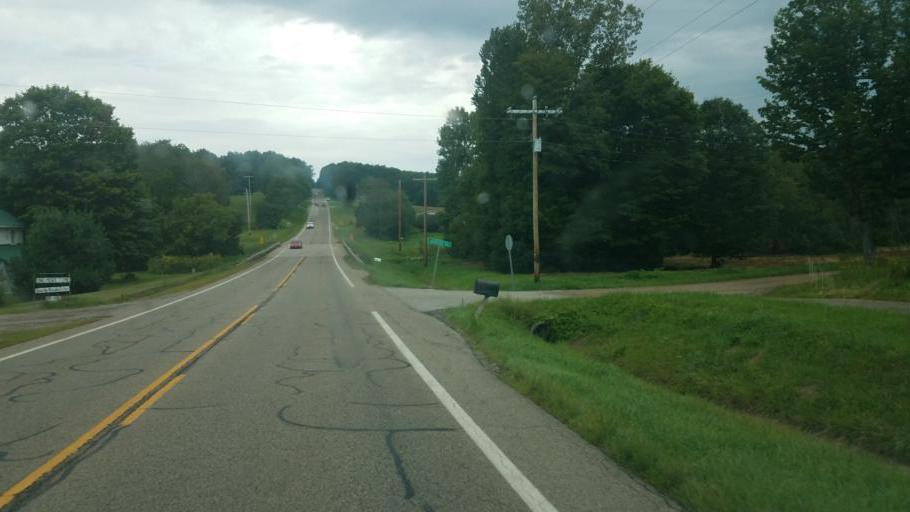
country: US
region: Ohio
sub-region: Knox County
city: Gambier
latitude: 40.4596
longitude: -82.4029
